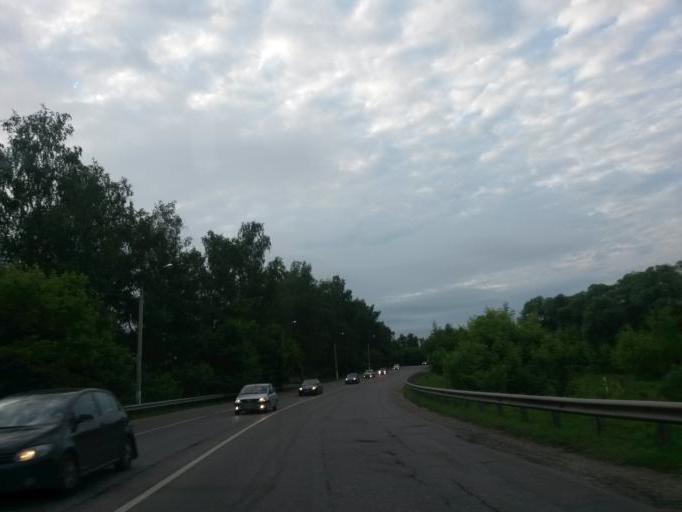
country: RU
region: Moskovskaya
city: Stolbovaya
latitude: 55.2181
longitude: 37.5029
